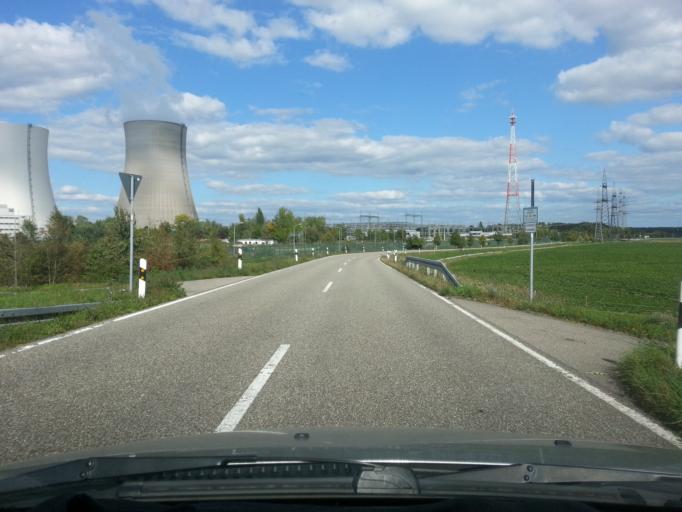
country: DE
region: Baden-Wuerttemberg
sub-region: Karlsruhe Region
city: Philippsburg
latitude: 49.2473
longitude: 8.4369
